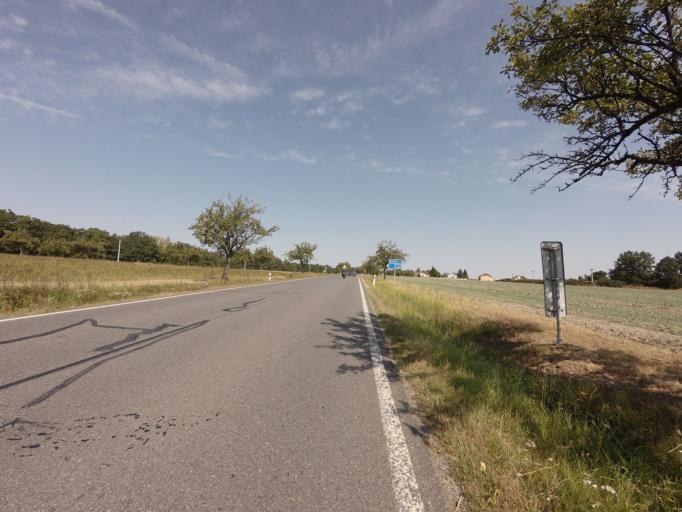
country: CZ
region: Jihocesky
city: Milevsko
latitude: 49.4109
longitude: 14.3595
